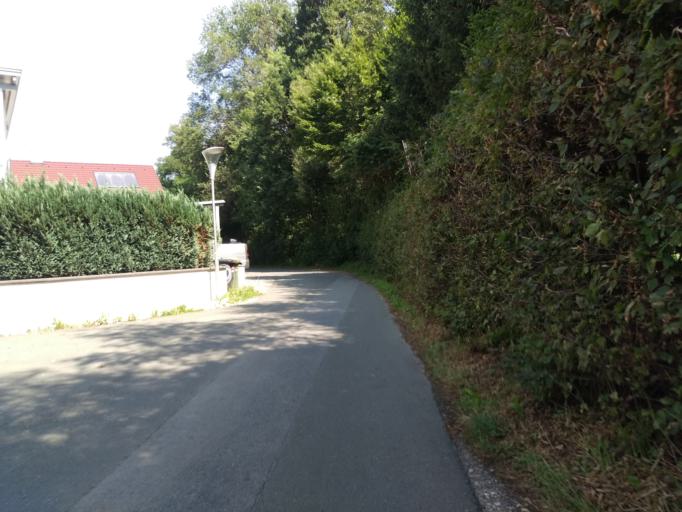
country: AT
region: Styria
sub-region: Politischer Bezirk Graz-Umgebung
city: Gossendorf
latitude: 46.9863
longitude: 15.4700
